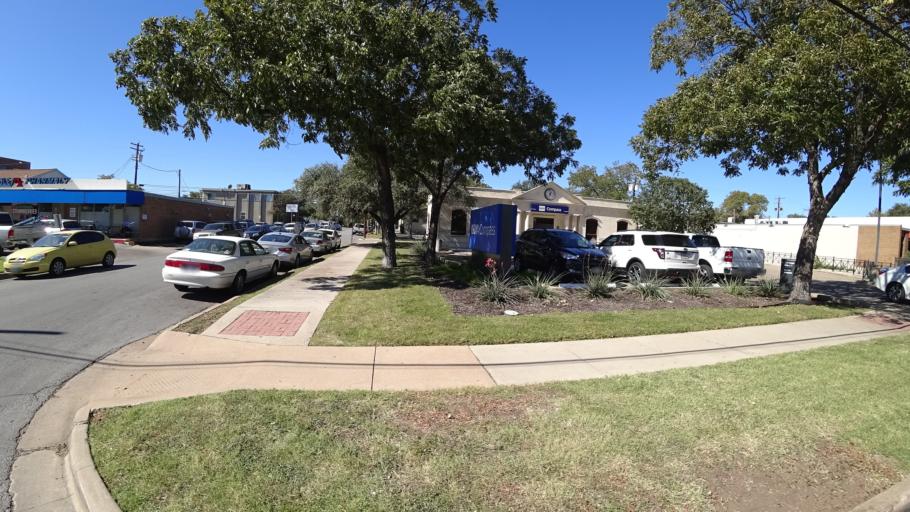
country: US
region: Texas
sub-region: Travis County
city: Austin
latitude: 30.3090
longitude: -97.7407
